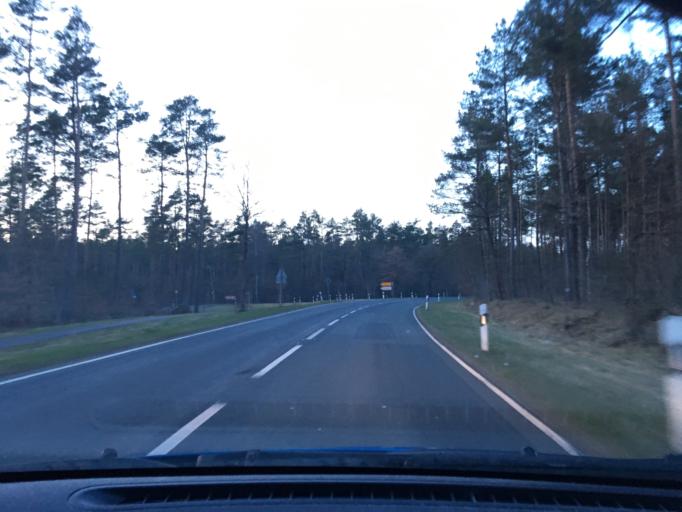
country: DE
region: Lower Saxony
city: Egestorf
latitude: 53.1713
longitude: 10.0588
